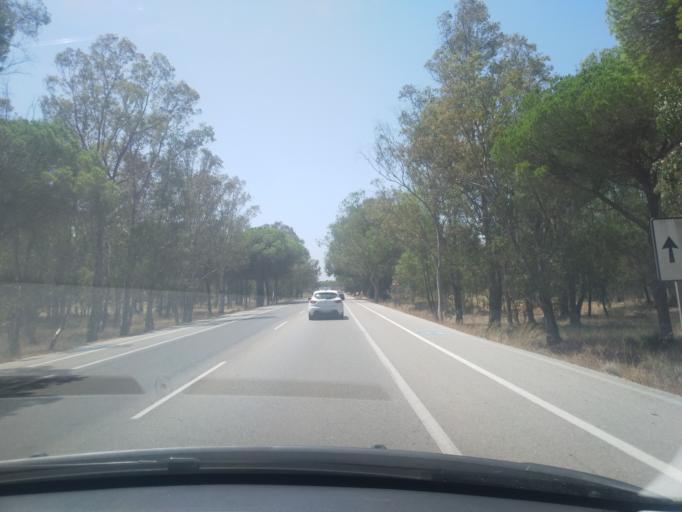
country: ES
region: Andalusia
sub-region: Provincia de Cadiz
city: Chiclana de la Frontera
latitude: 36.3906
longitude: -6.1285
